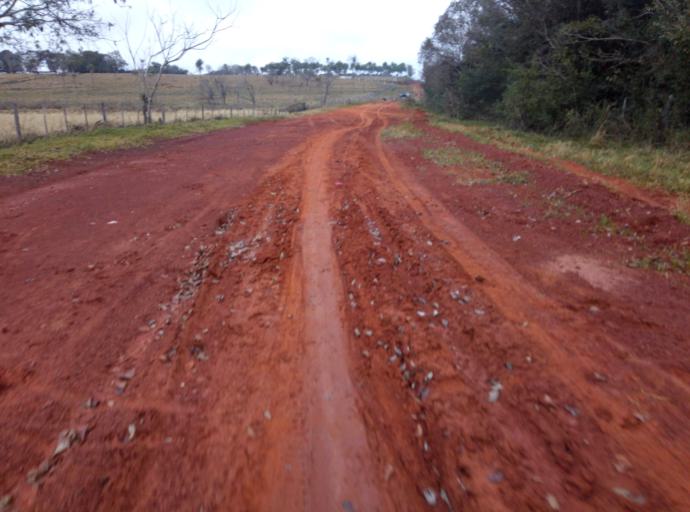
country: PY
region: Caaguazu
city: Doctor Cecilio Baez
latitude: -25.1224
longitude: -56.2095
